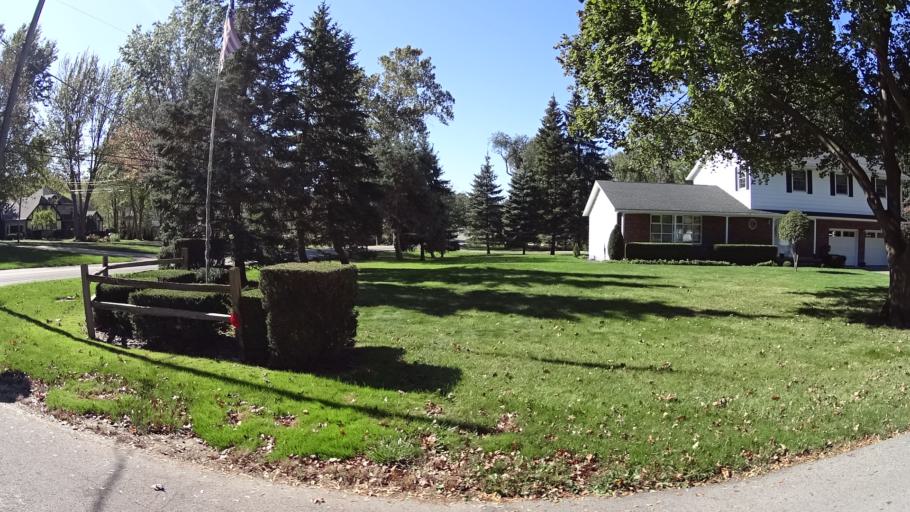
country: US
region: Ohio
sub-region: Lorain County
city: Amherst
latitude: 41.3983
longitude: -82.2060
